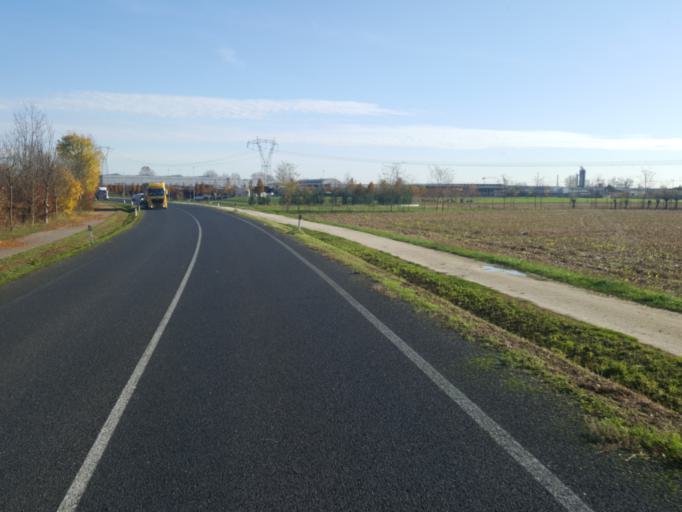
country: IT
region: Veneto
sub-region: Provincia di Treviso
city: Riese Pio X
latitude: 45.7179
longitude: 11.9147
